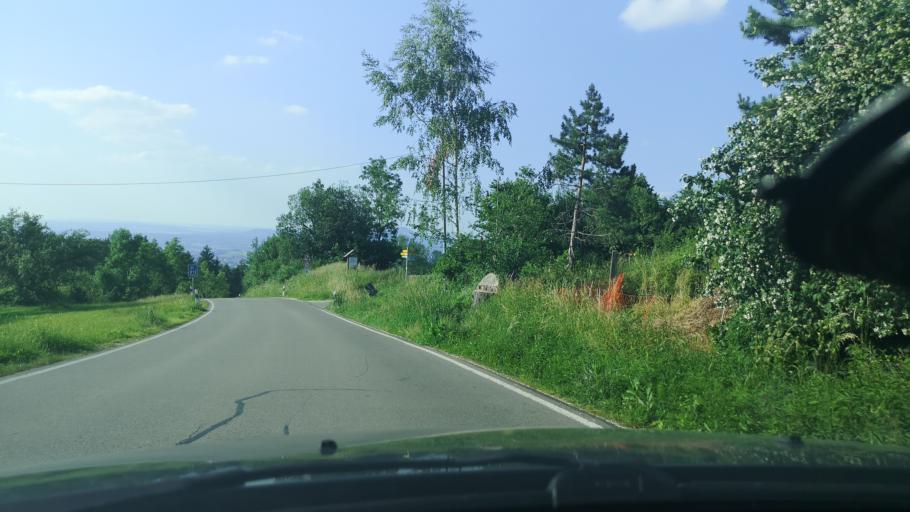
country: DE
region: Baden-Wuerttemberg
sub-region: Regierungsbezirk Stuttgart
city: Schlat
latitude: 48.6349
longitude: 9.7040
